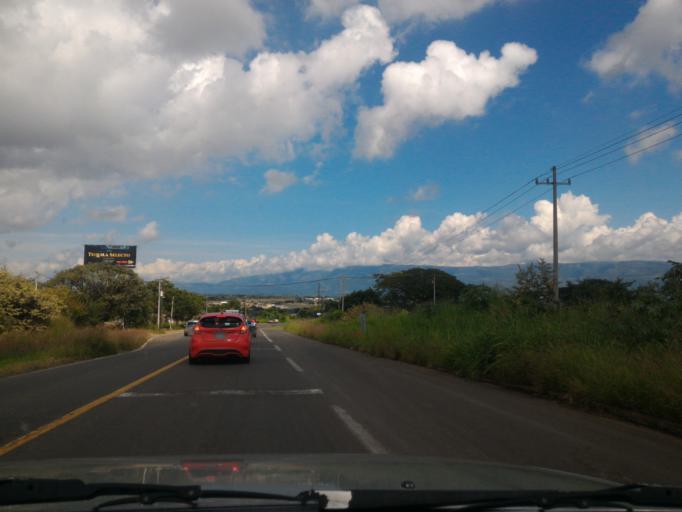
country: MX
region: Jalisco
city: Amatitan
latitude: 20.8346
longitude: -103.7229
